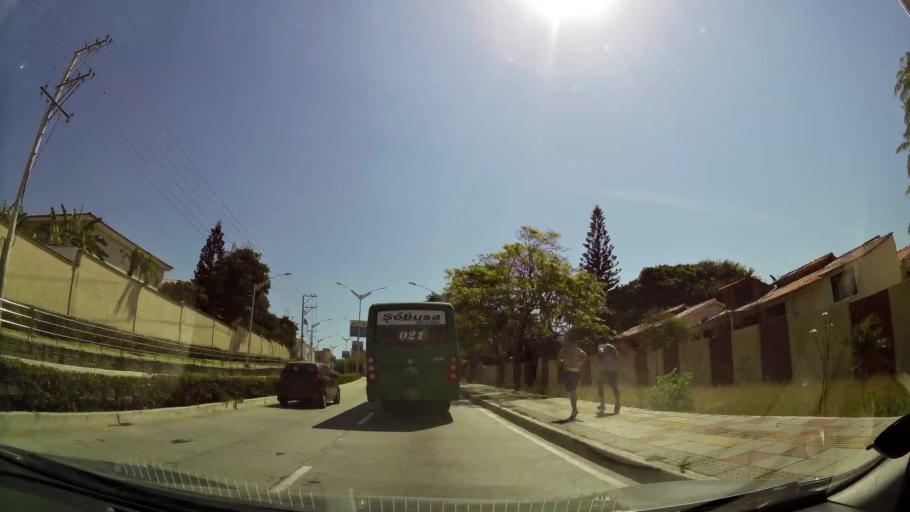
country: CO
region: Atlantico
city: Barranquilla
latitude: 11.0117
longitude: -74.8317
